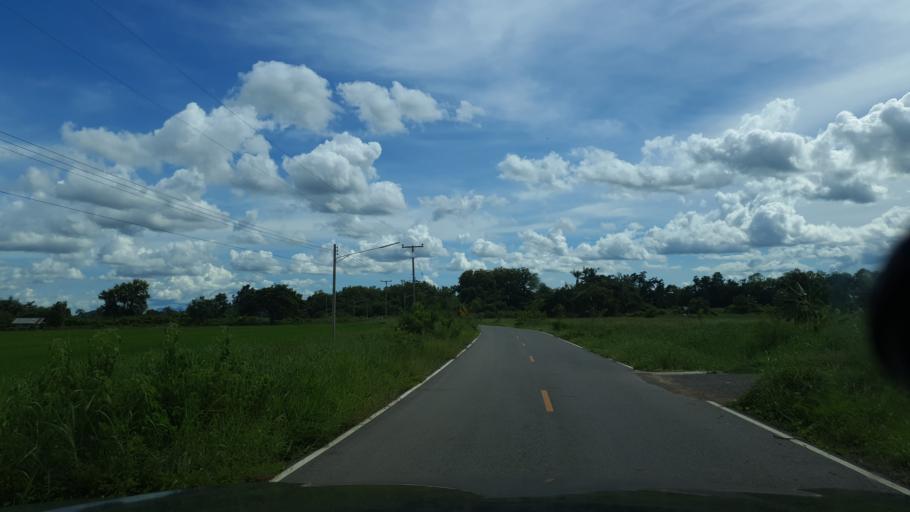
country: TH
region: Sukhothai
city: Thung Saliam
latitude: 17.3516
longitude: 99.6409
